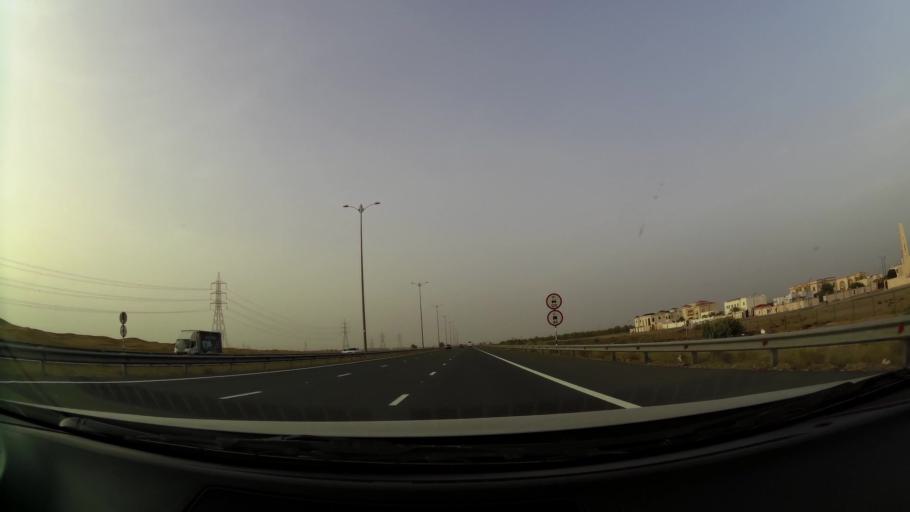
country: OM
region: Al Buraimi
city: Al Buraymi
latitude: 24.3639
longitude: 55.7902
